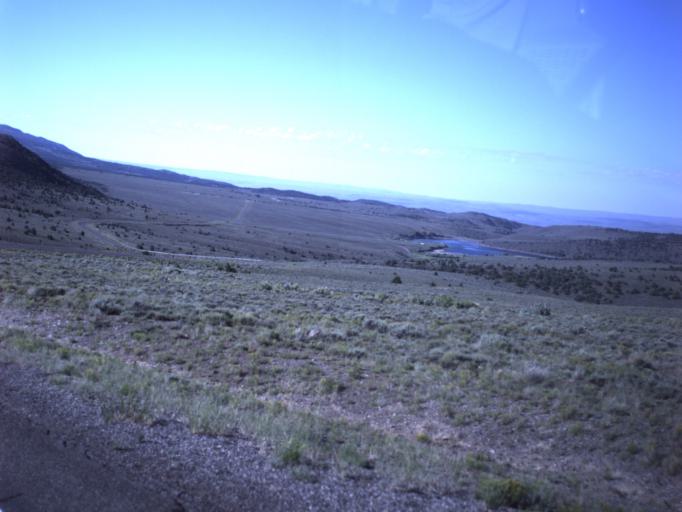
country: US
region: Utah
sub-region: Wayne County
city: Loa
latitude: 38.5404
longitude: -111.5124
